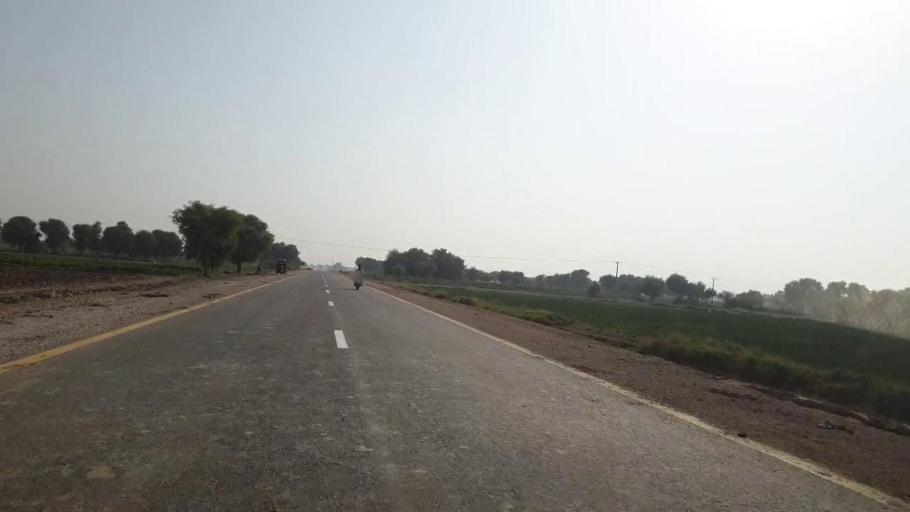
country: PK
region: Sindh
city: Bhan
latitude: 26.5212
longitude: 67.7878
